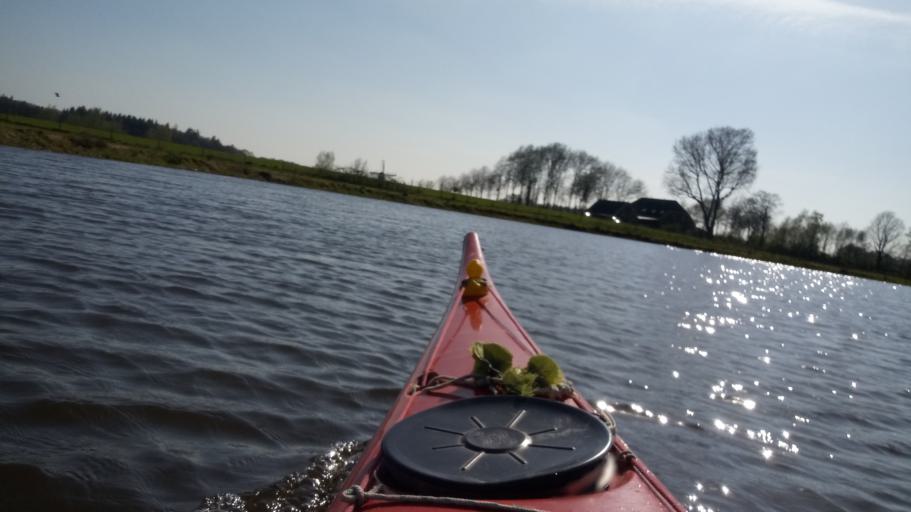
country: NL
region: Gelderland
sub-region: Gemeente Lochem
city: Almen
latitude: 52.1517
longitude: 6.2817
